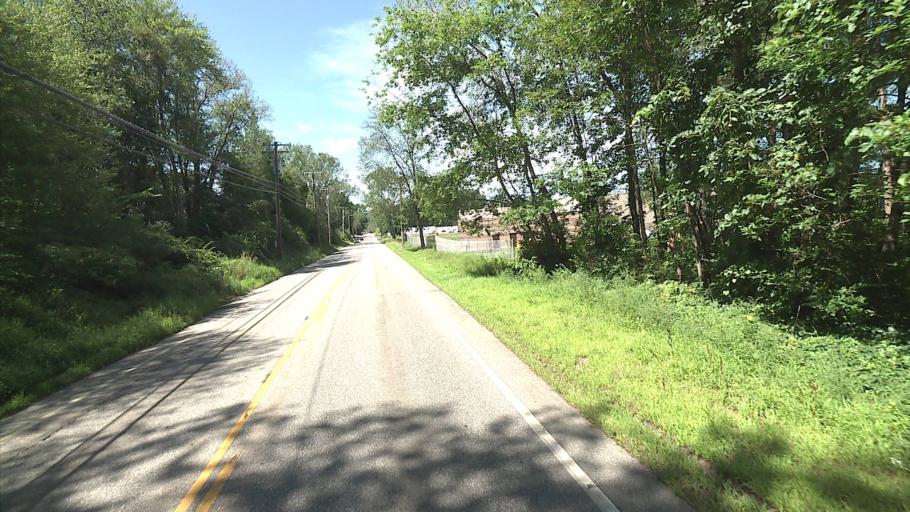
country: US
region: Connecticut
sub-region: Windham County
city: Putnam
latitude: 41.8554
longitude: -71.9549
